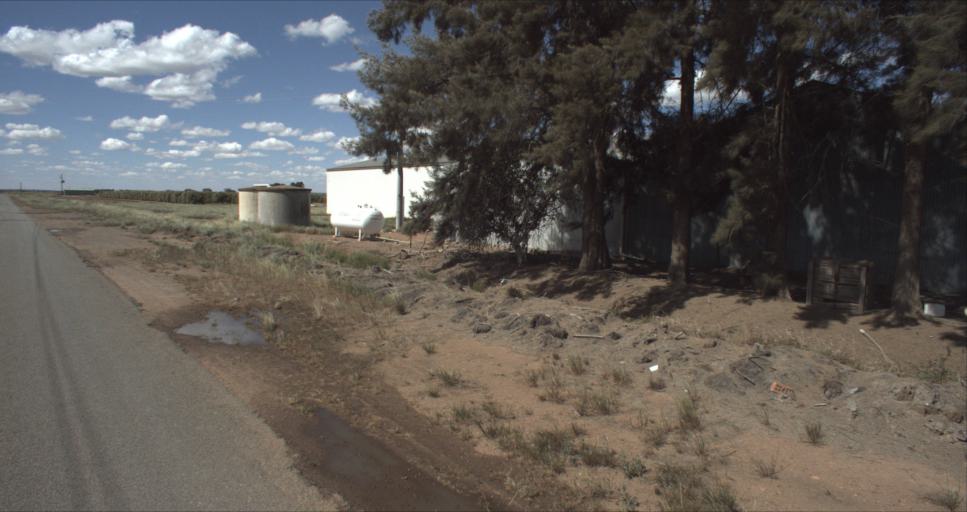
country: AU
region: New South Wales
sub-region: Leeton
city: Leeton
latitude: -34.5114
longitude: 146.2530
